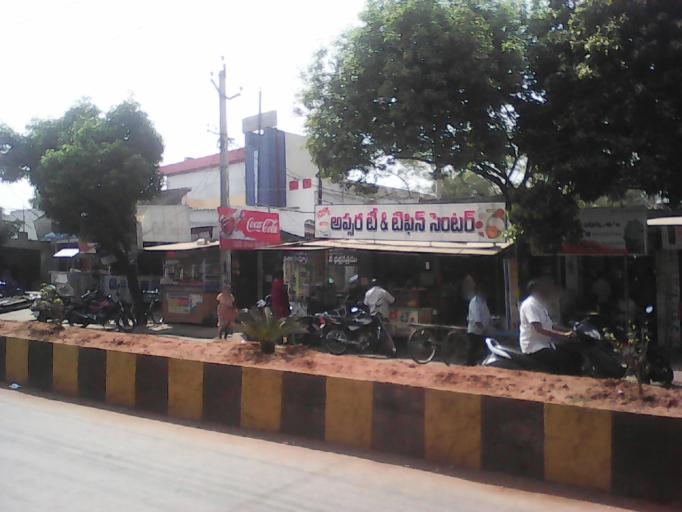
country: IN
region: Andhra Pradesh
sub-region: Guntur
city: Bhattiprolu
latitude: 16.2353
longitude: 80.6500
